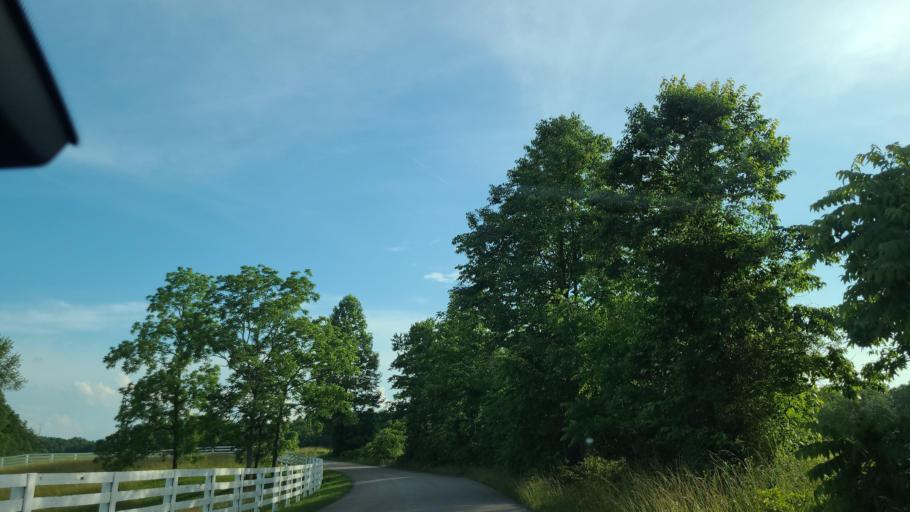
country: US
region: Kentucky
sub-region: Whitley County
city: Corbin
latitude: 36.8924
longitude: -84.2330
